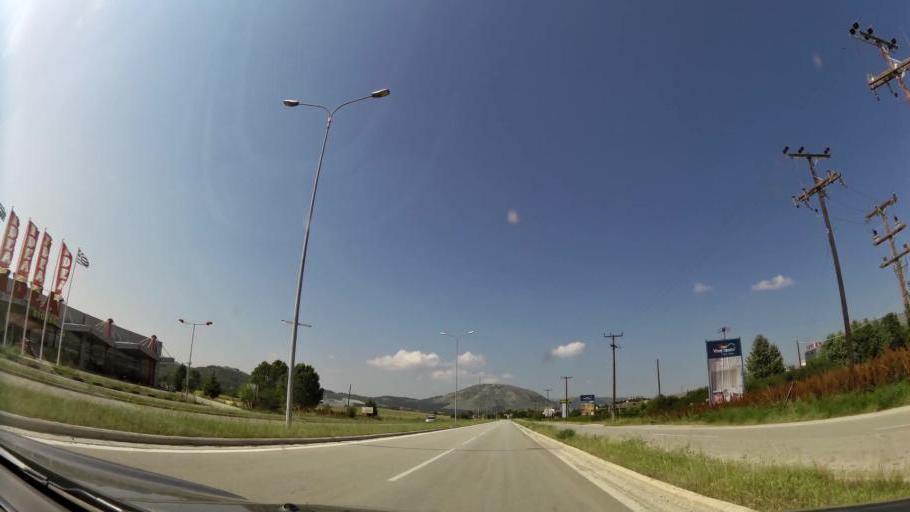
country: GR
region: West Macedonia
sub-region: Nomos Kozanis
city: Koila
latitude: 40.3431
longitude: 21.7964
